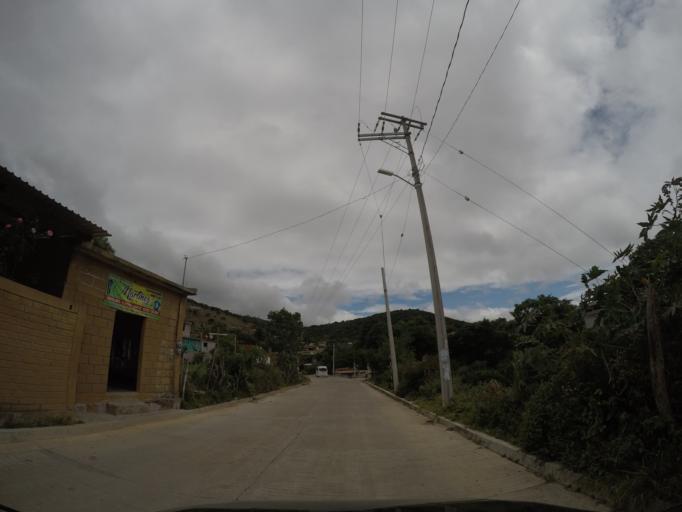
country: MX
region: Oaxaca
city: San Lorenzo Albarradas
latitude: 16.9124
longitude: -96.2583
